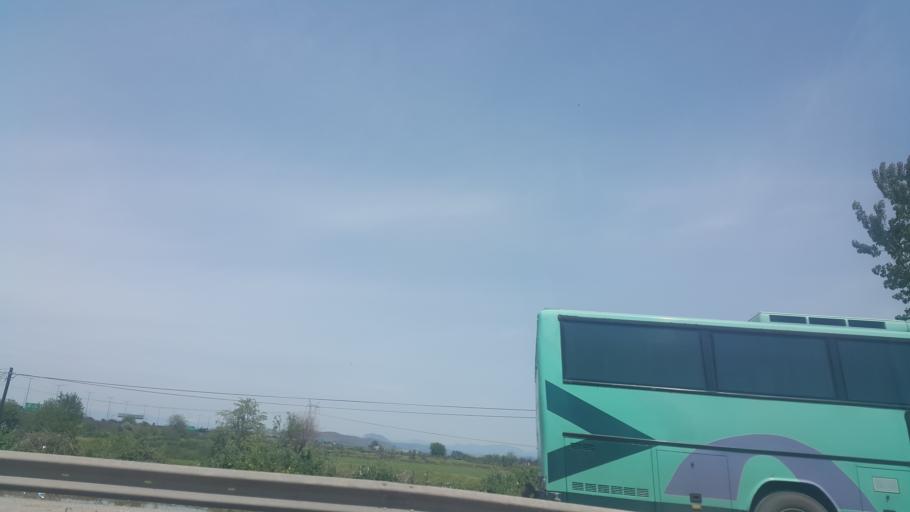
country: TR
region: Osmaniye
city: Toprakkale
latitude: 37.0620
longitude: 36.1113
